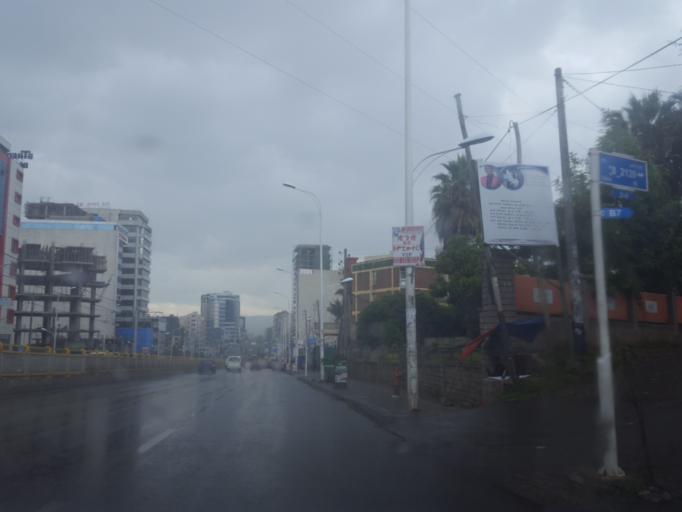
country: ET
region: Adis Abeba
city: Addis Ababa
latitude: 9.0171
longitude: 38.7927
